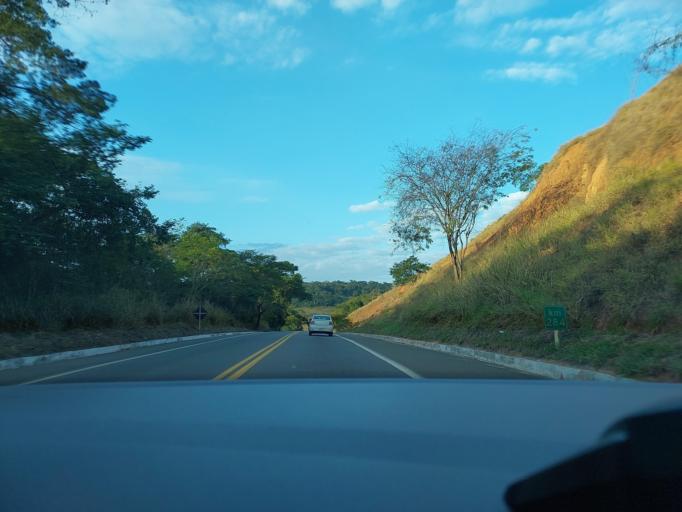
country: BR
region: Minas Gerais
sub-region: Muriae
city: Muriae
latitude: -21.1225
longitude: -42.2154
